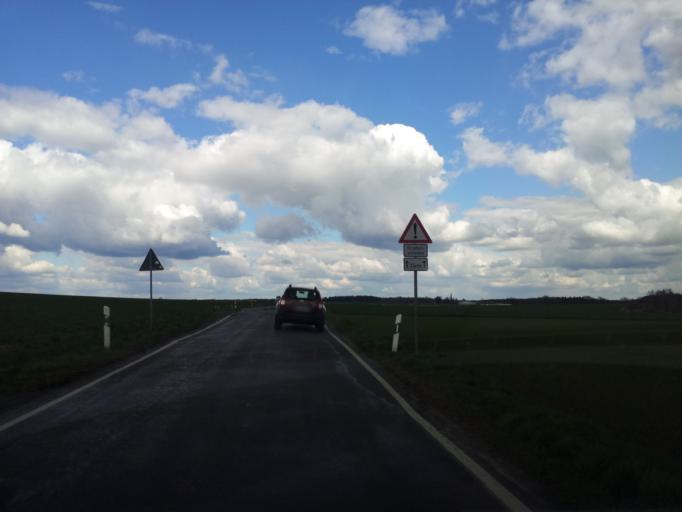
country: DE
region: Saxony
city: Nebelschutz
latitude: 51.2544
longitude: 14.1836
